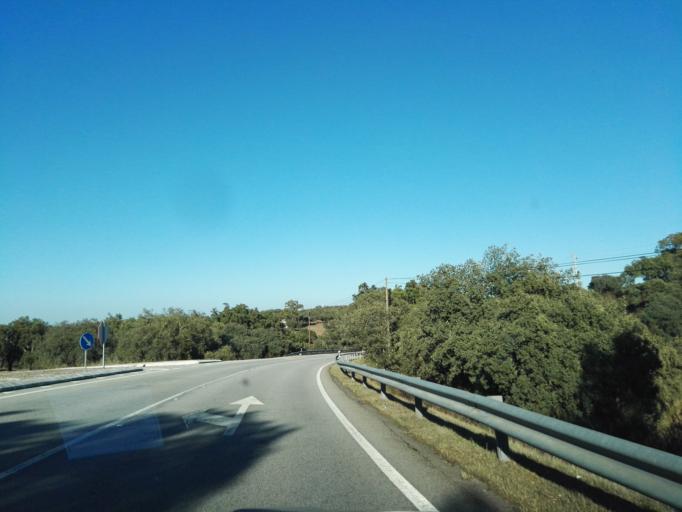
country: PT
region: Evora
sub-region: Estremoz
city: Estremoz
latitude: 38.7815
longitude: -7.6957
